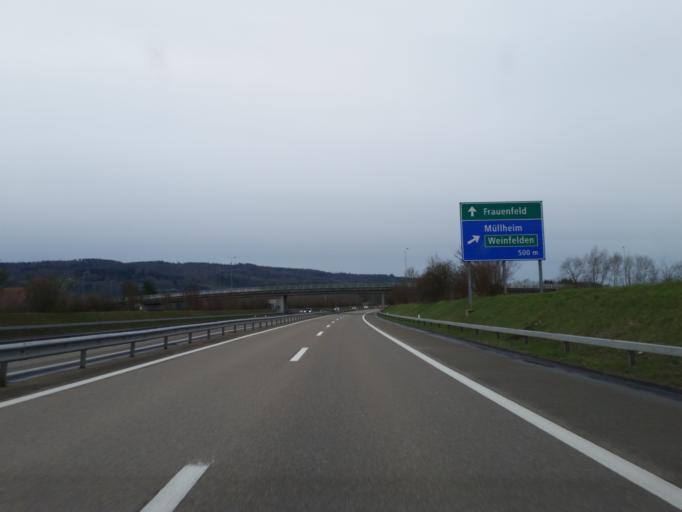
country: CH
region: Thurgau
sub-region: Frauenfeld District
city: Mullheim
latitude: 47.5958
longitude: 9.0085
